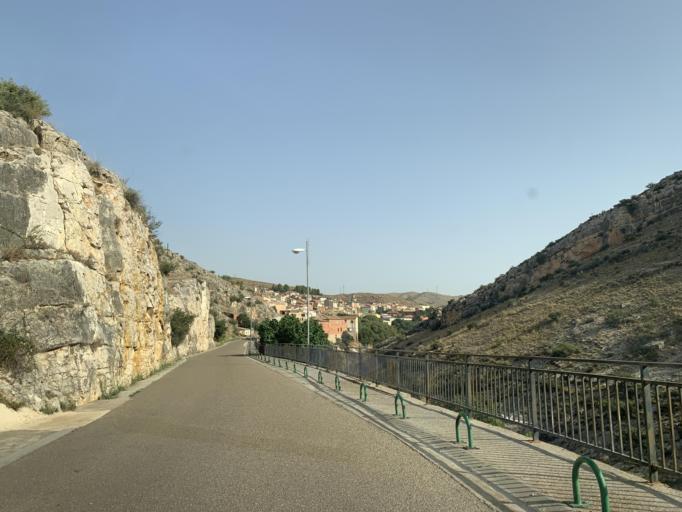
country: ES
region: Aragon
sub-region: Provincia de Zaragoza
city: Almonacid de la Cuba
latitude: 41.2764
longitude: -0.7907
